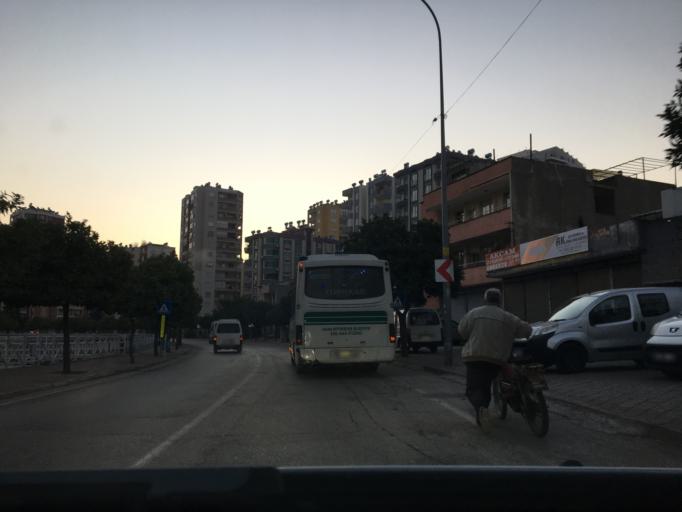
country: TR
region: Adana
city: Seyhan
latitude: 37.0282
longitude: 35.2835
